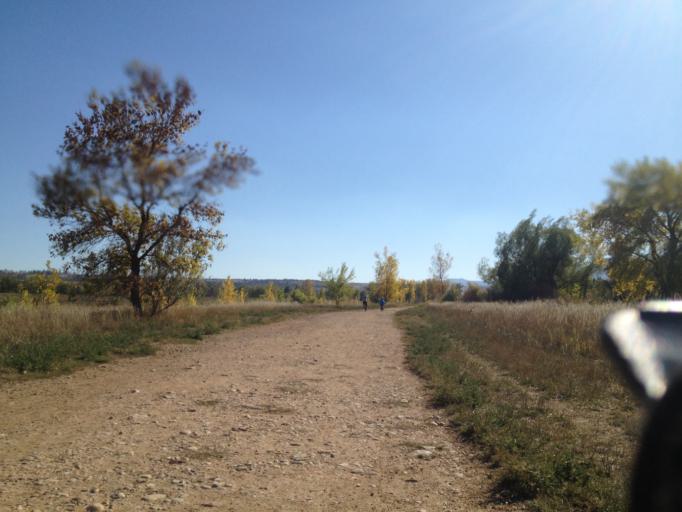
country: US
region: Colorado
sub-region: Boulder County
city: Boulder
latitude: 39.9756
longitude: -105.2334
